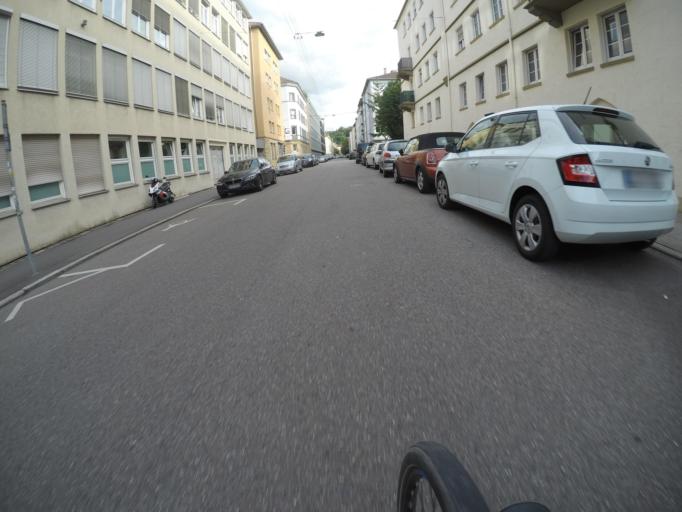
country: DE
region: Baden-Wuerttemberg
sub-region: Regierungsbezirk Stuttgart
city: Stuttgart
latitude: 48.7745
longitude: 9.1614
